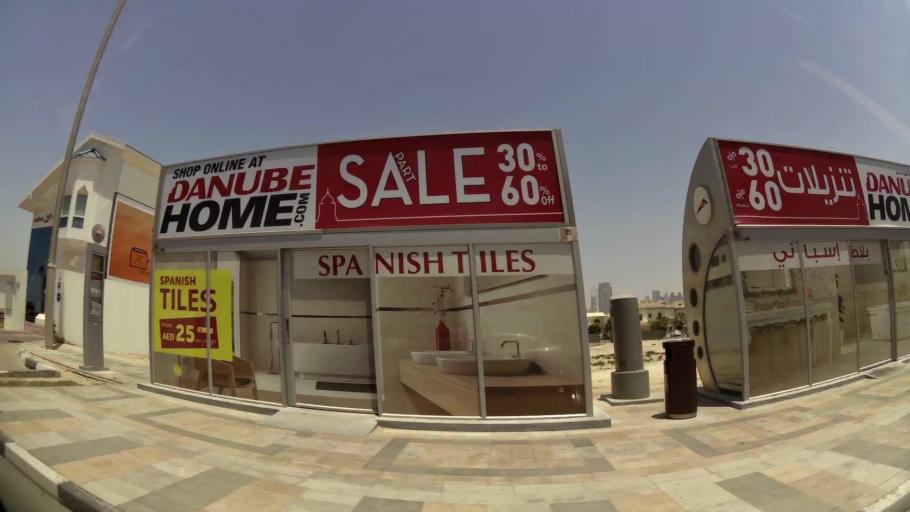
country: AE
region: Dubai
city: Dubai
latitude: 25.2262
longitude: 55.2592
